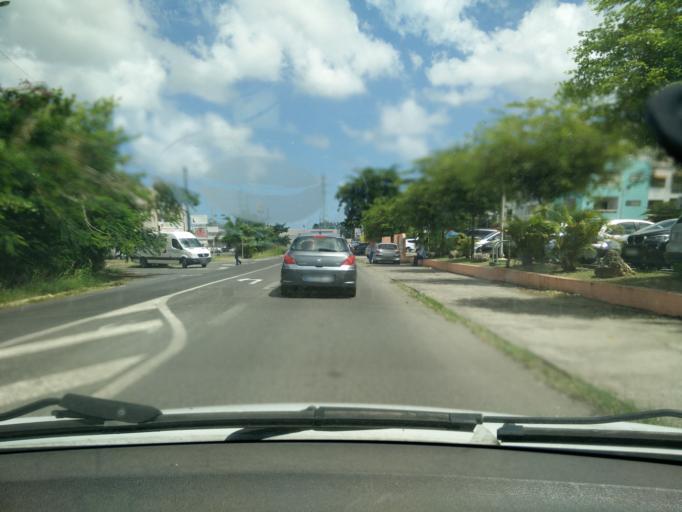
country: GP
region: Guadeloupe
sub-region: Guadeloupe
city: Pointe-a-Pitre
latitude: 16.2528
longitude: -61.5218
